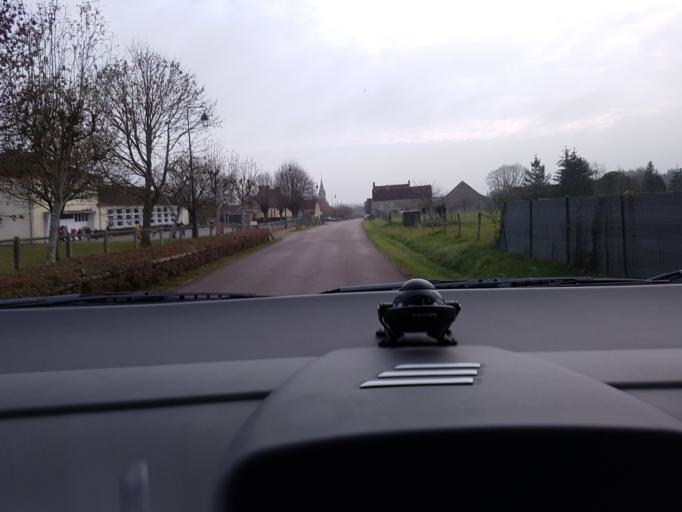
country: FR
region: Lower Normandy
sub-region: Departement de l'Orne
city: Mortree
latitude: 48.6341
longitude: 0.0325
